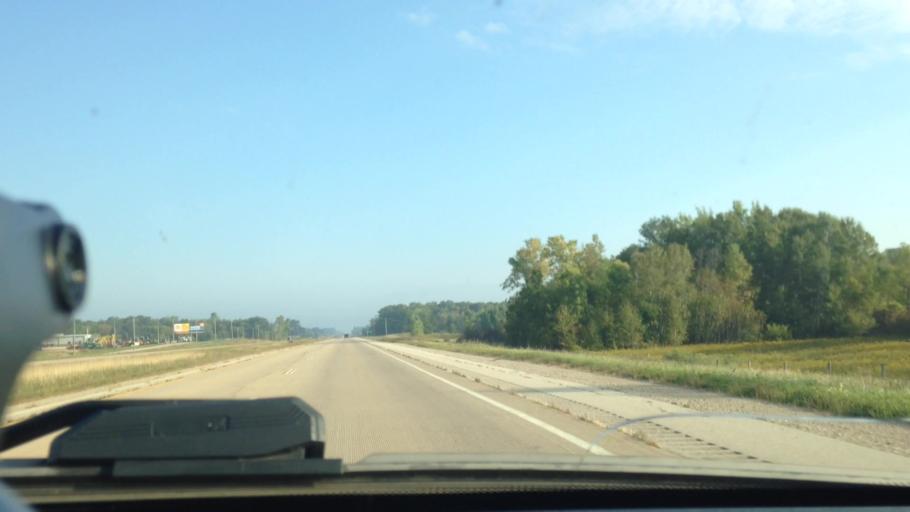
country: US
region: Wisconsin
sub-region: Oconto County
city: Oconto Falls
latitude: 44.9956
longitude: -88.0451
